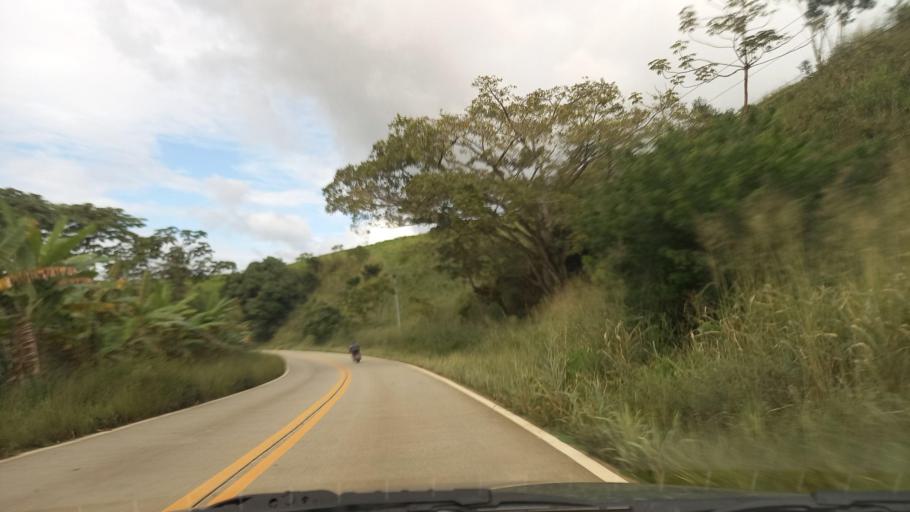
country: BR
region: Pernambuco
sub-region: Maraial
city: Maraial
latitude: -8.7550
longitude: -35.8441
